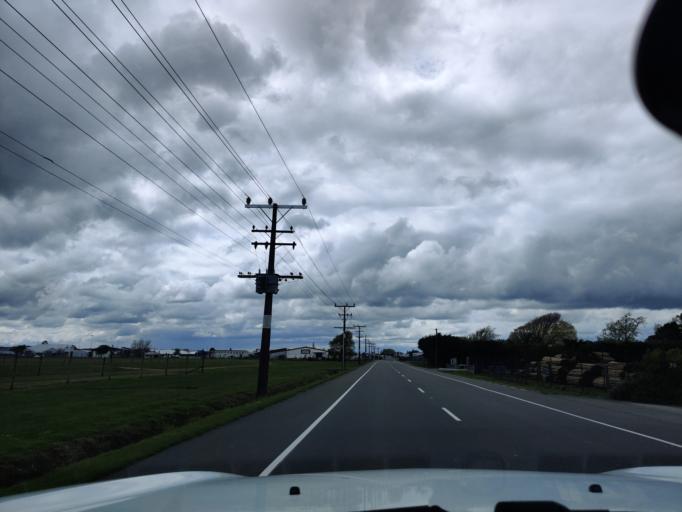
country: NZ
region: Manawatu-Wanganui
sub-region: Palmerston North City
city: Palmerston North
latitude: -40.2339
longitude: 175.5653
